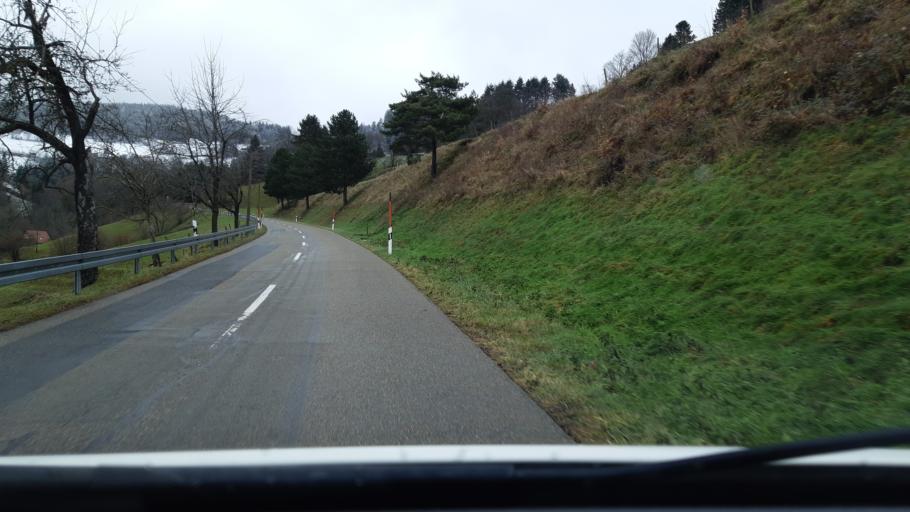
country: DE
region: Baden-Wuerttemberg
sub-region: Freiburg Region
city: Solden
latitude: 47.9099
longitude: 7.8413
